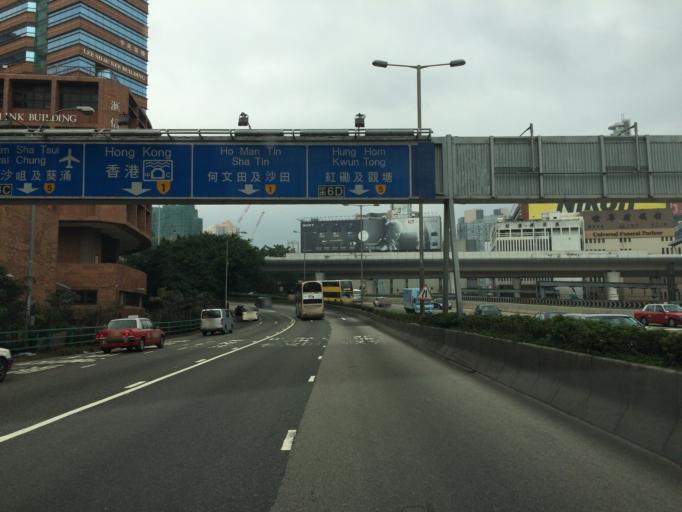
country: HK
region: Kowloon City
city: Kowloon
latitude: 22.3047
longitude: 114.1811
